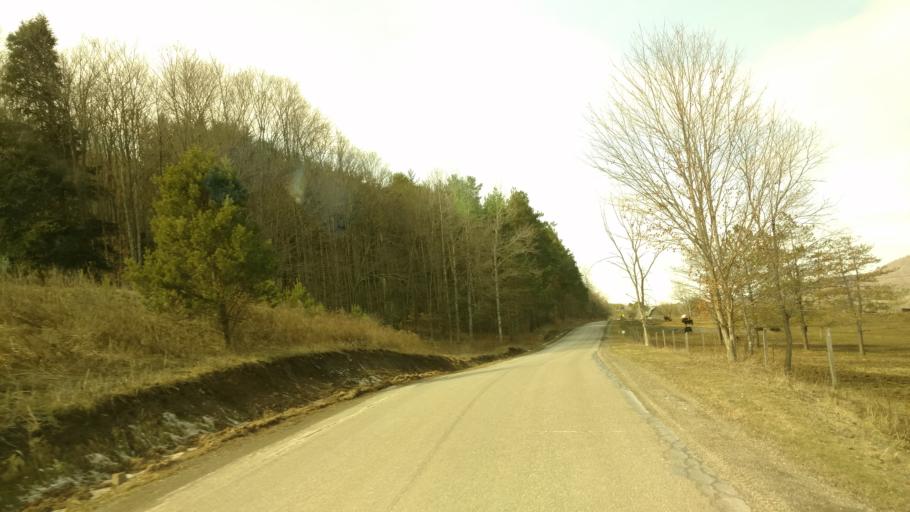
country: US
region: New York
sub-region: Allegany County
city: Wellsville
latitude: 41.9571
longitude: -77.8374
